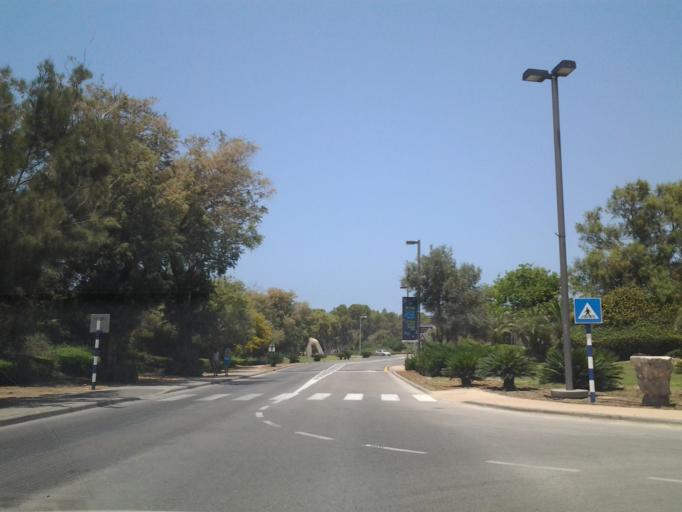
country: IL
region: Haifa
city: Qesarya
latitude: 32.5042
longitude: 34.9045
